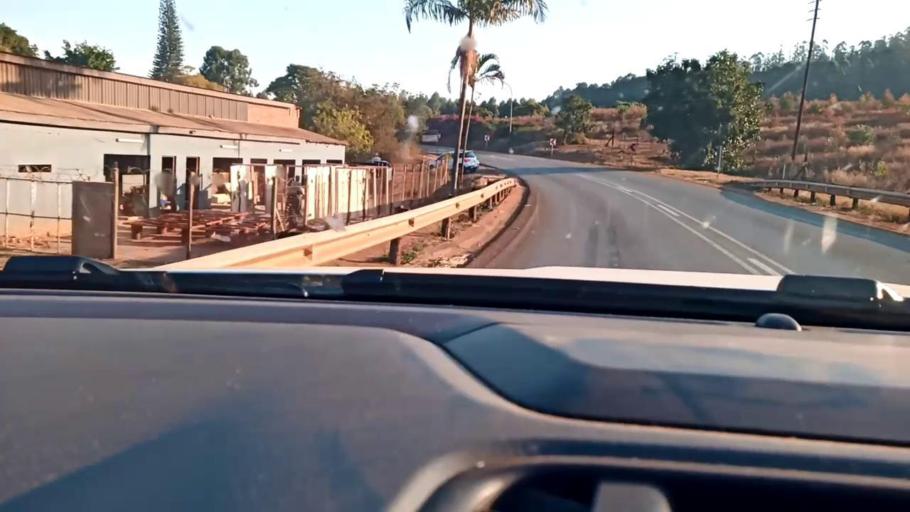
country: ZA
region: Limpopo
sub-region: Mopani District Municipality
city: Duiwelskloof
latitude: -23.6989
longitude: 30.1369
